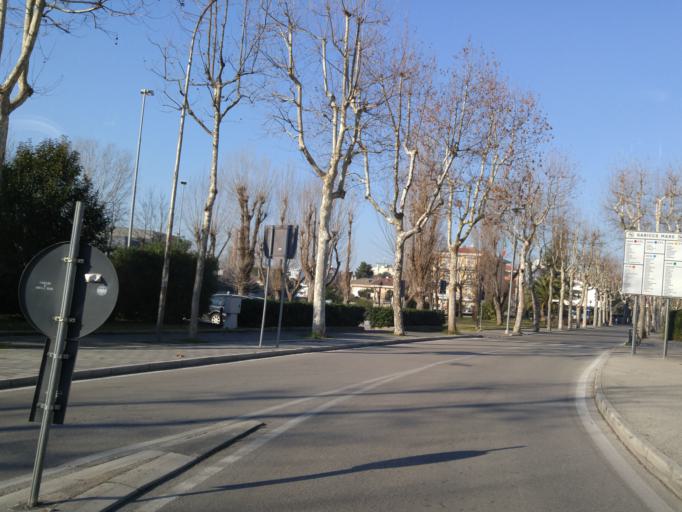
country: IT
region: The Marches
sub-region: Provincia di Pesaro e Urbino
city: Gabicce Mare
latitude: 43.9626
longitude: 12.7567
